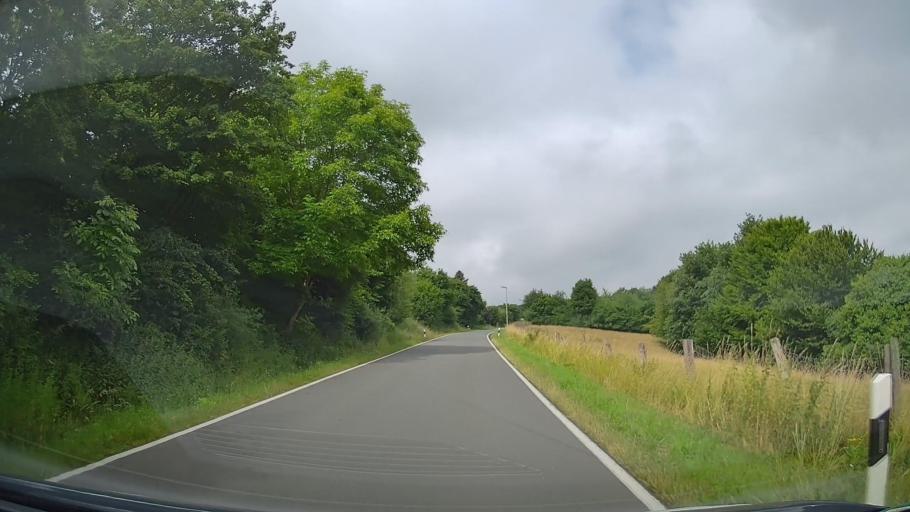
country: DE
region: Lower Saxony
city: Rinteln
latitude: 52.1269
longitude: 9.1054
